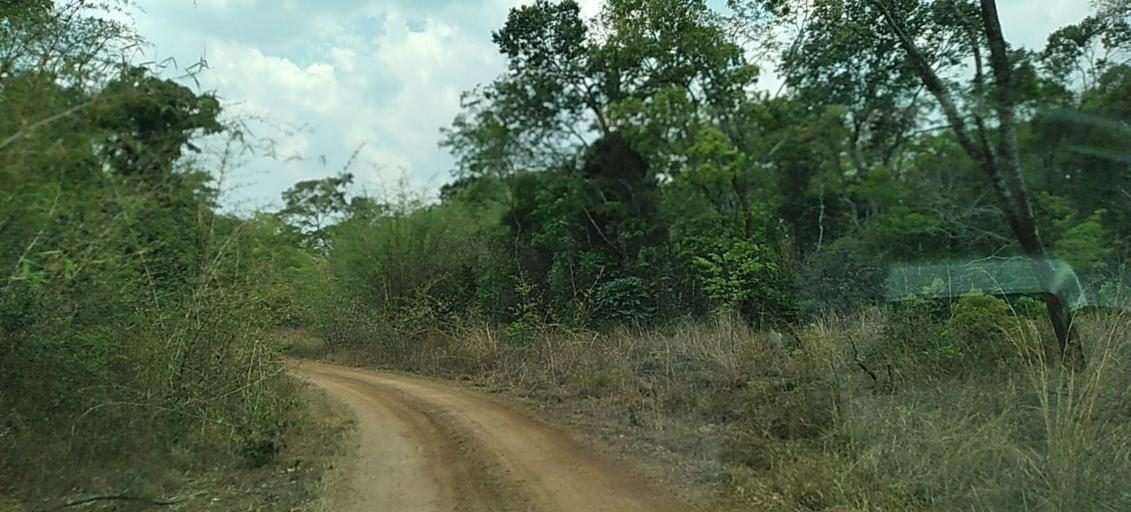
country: ZM
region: Copperbelt
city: Chingola
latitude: -12.8039
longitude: 27.6414
